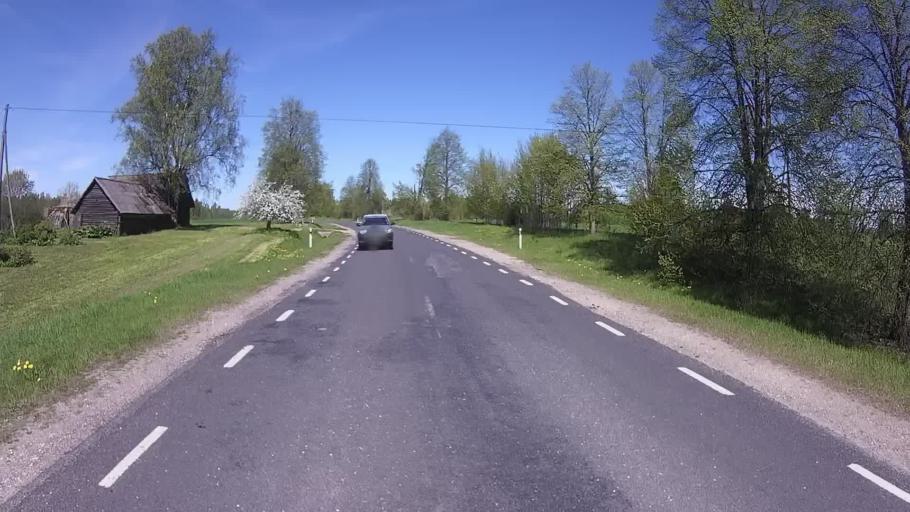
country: EE
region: Polvamaa
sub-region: Raepina vald
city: Rapina
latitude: 58.0403
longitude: 27.3928
